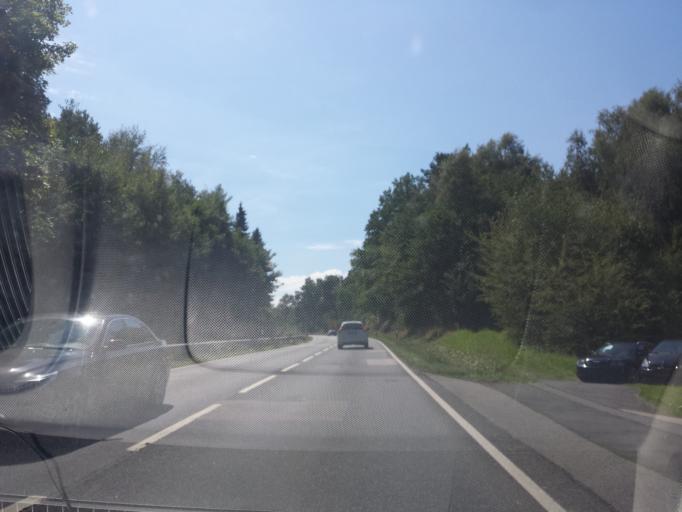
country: DE
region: Bavaria
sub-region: Upper Palatinate
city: Traitsching
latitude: 49.1265
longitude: 12.6518
